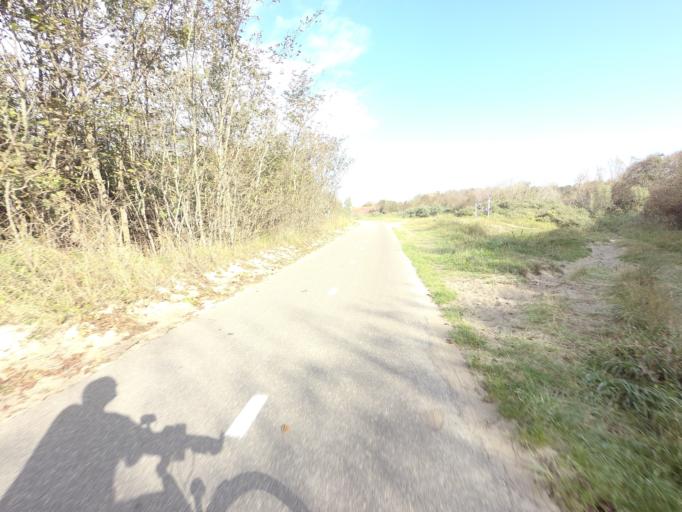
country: NL
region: Zeeland
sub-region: Gemeente Vlissingen
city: Vlissingen
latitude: 51.4937
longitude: 3.5012
